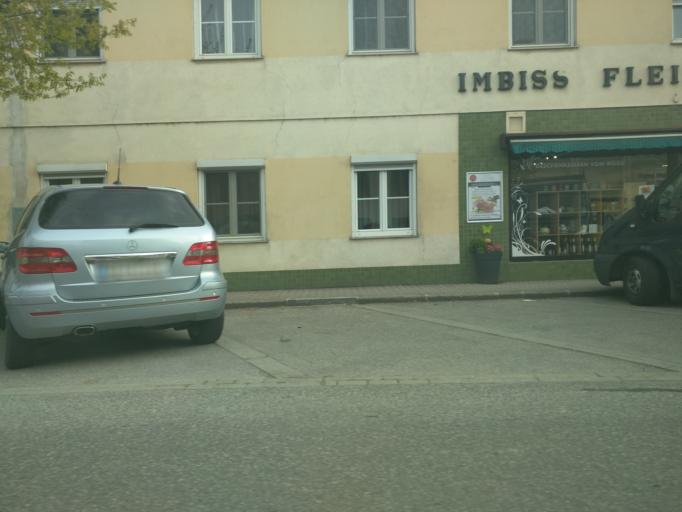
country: AT
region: Lower Austria
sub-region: Politischer Bezirk Melk
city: Blindenmarkt
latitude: 48.1284
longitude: 14.9879
